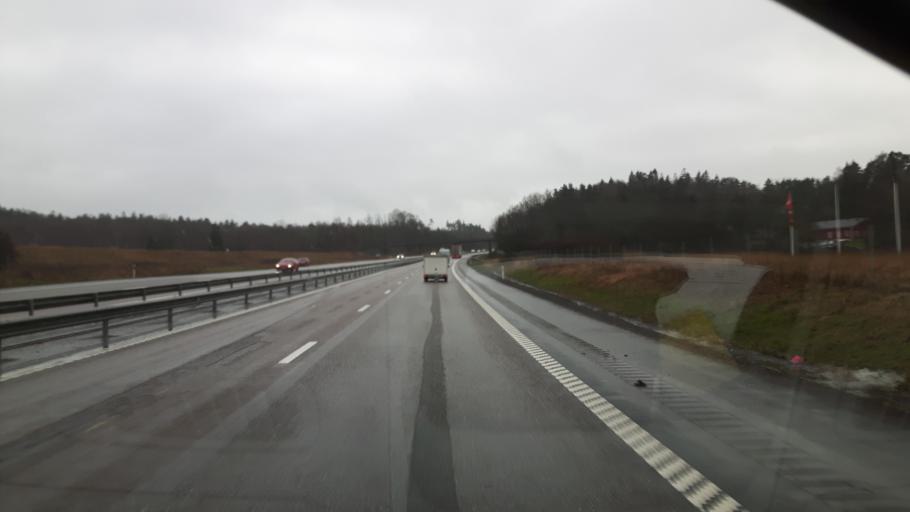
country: SE
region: Halland
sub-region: Kungsbacka Kommun
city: Kungsbacka
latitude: 57.5044
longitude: 12.0526
